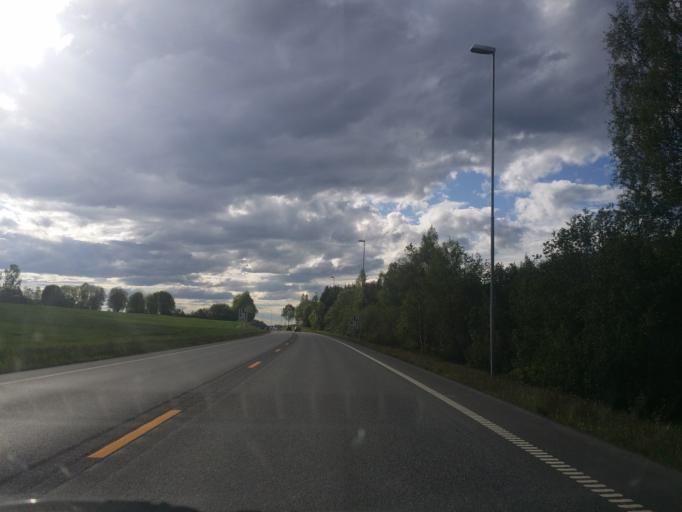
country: NO
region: Hedmark
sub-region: Stange
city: Stange
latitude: 60.7671
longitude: 11.1775
